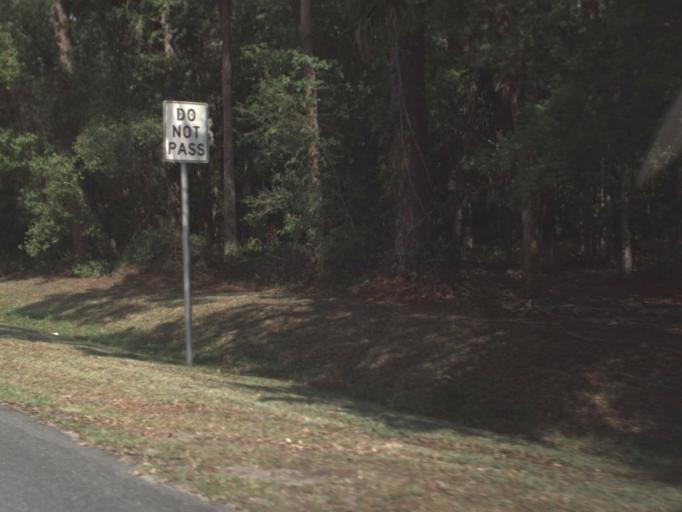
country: US
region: Florida
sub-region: Lake County
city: Astor
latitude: 29.1626
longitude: -81.5313
